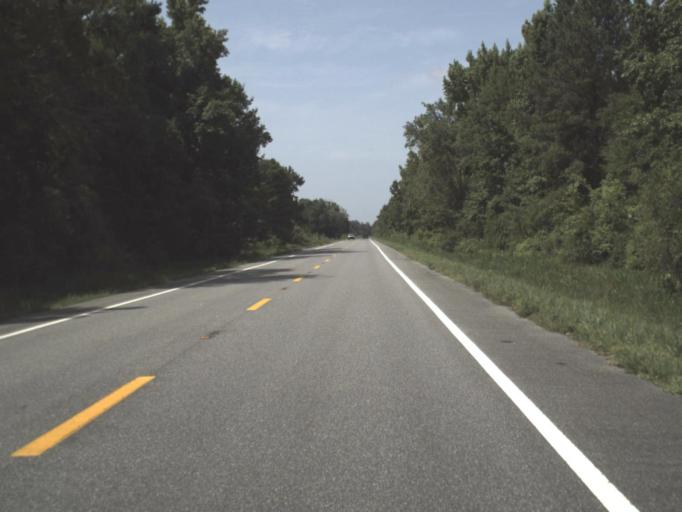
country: US
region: Florida
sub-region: Taylor County
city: Steinhatchee
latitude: 29.8699
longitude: -83.3075
